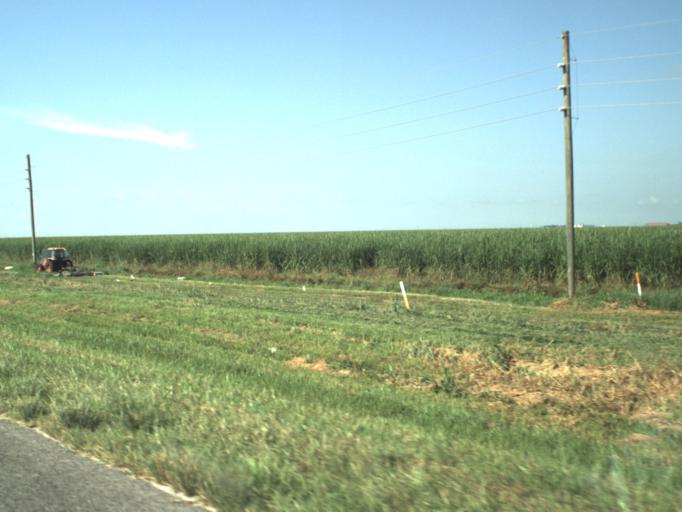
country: US
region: Florida
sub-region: Palm Beach County
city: South Bay
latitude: 26.5985
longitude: -80.7115
